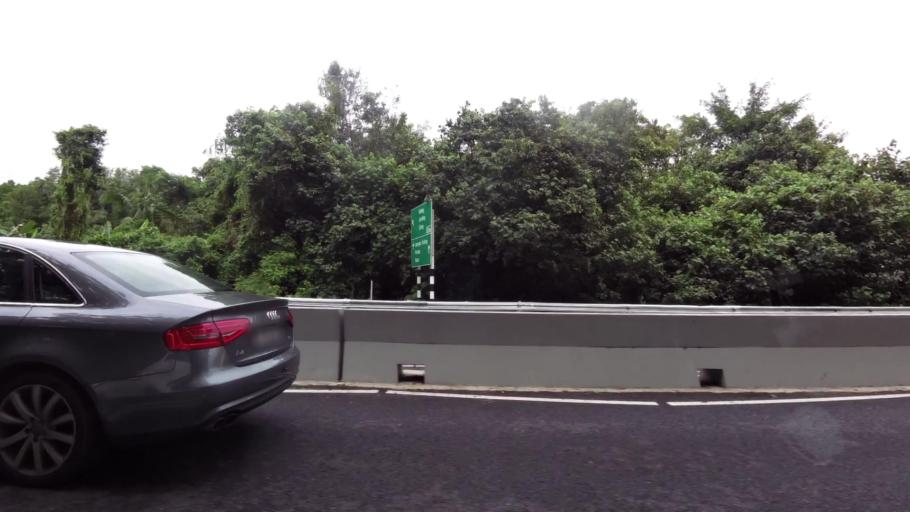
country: BN
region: Brunei and Muara
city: Bandar Seri Begawan
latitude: 4.9030
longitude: 114.9319
